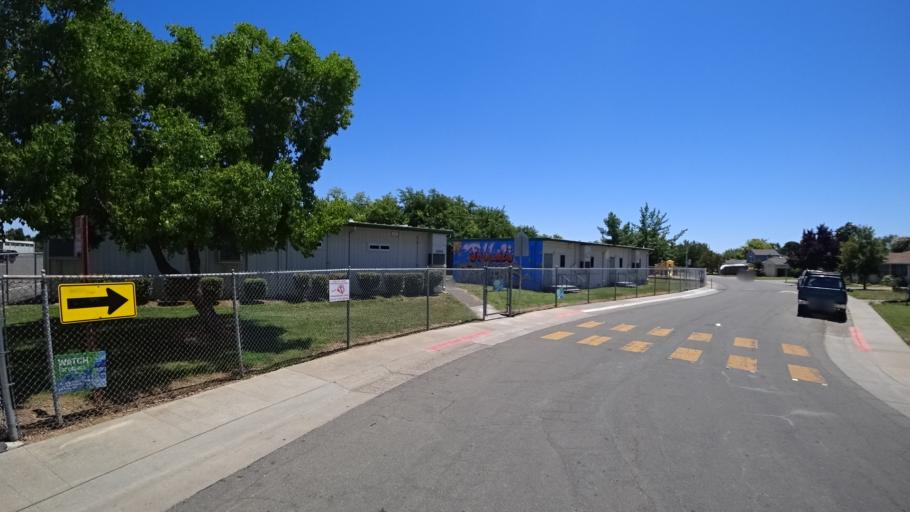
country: US
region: California
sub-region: Sacramento County
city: Parkway
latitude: 38.5303
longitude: -121.4908
